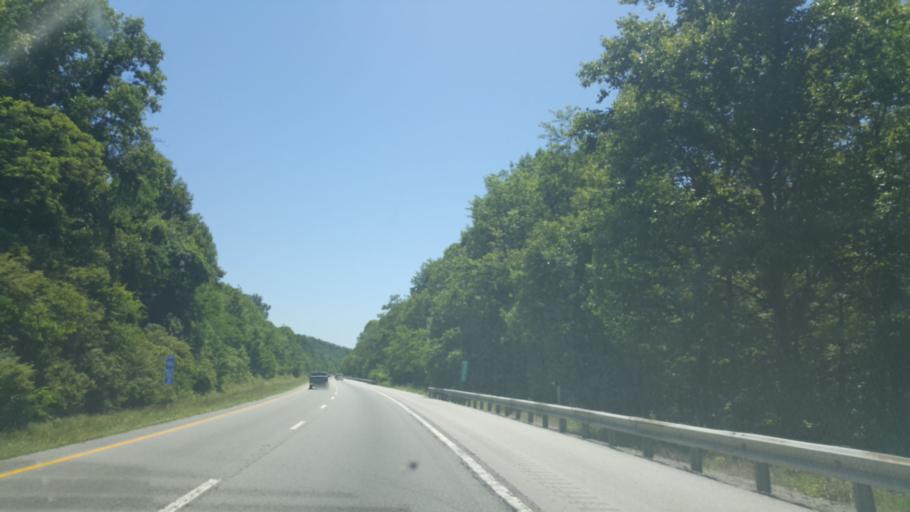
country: US
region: Tennessee
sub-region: Cumberland County
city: Fairfield Glade
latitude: 35.8881
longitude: -84.8372
